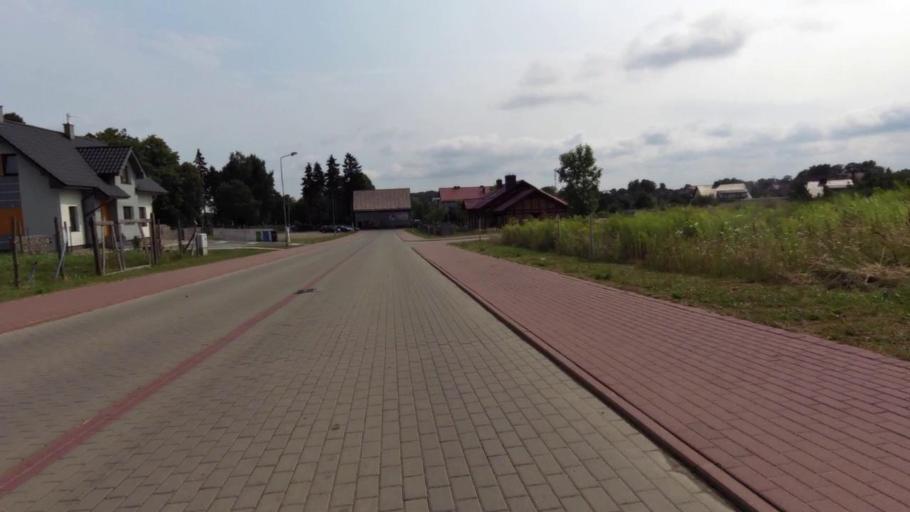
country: PL
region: West Pomeranian Voivodeship
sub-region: Powiat drawski
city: Czaplinek
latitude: 53.5635
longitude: 16.2359
